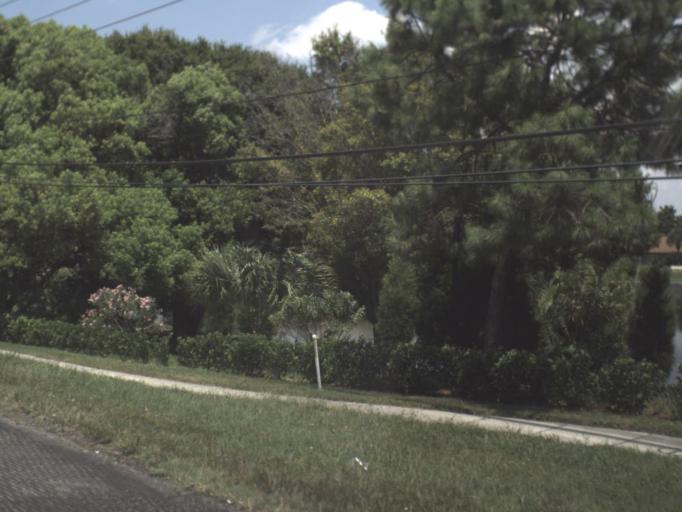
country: US
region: Florida
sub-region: Pinellas County
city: Palm Harbor
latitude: 28.0839
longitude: -82.7391
